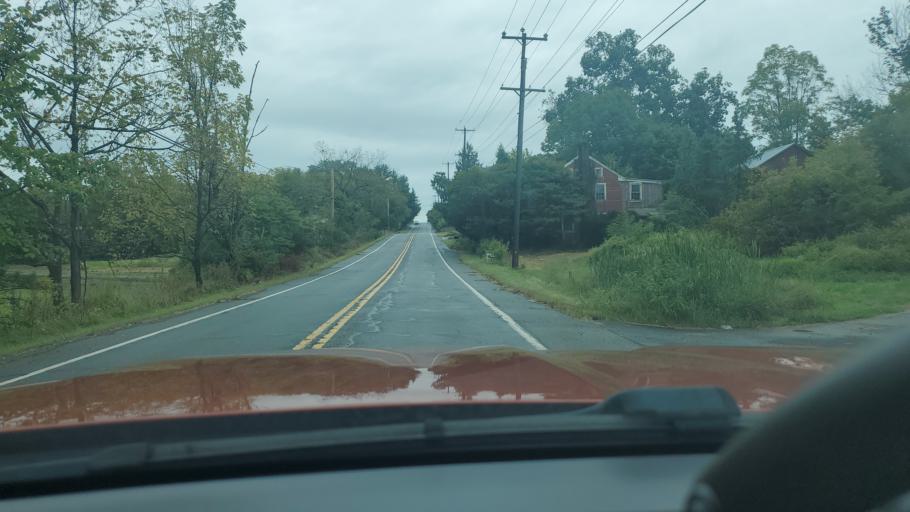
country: US
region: Pennsylvania
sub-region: Montgomery County
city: Spring Mount
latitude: 40.2869
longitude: -75.4814
